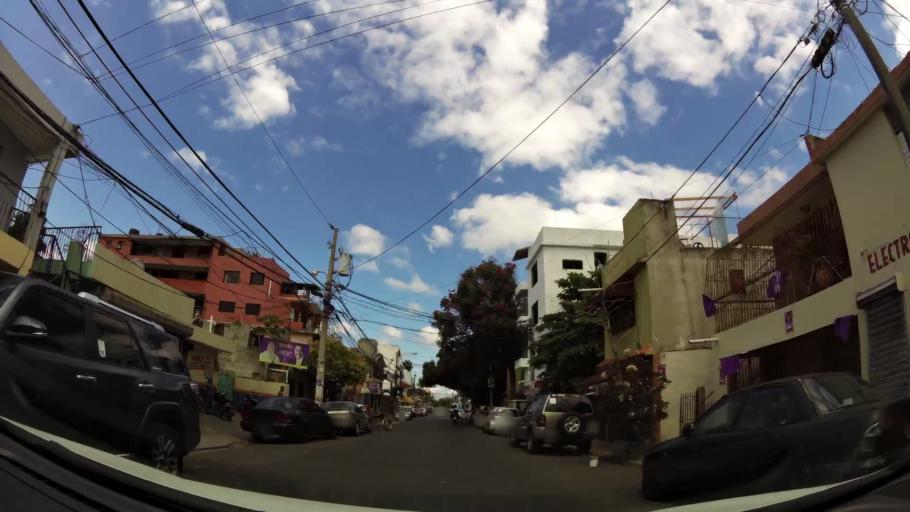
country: DO
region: Nacional
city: Bella Vista
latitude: 18.4644
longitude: -69.9466
